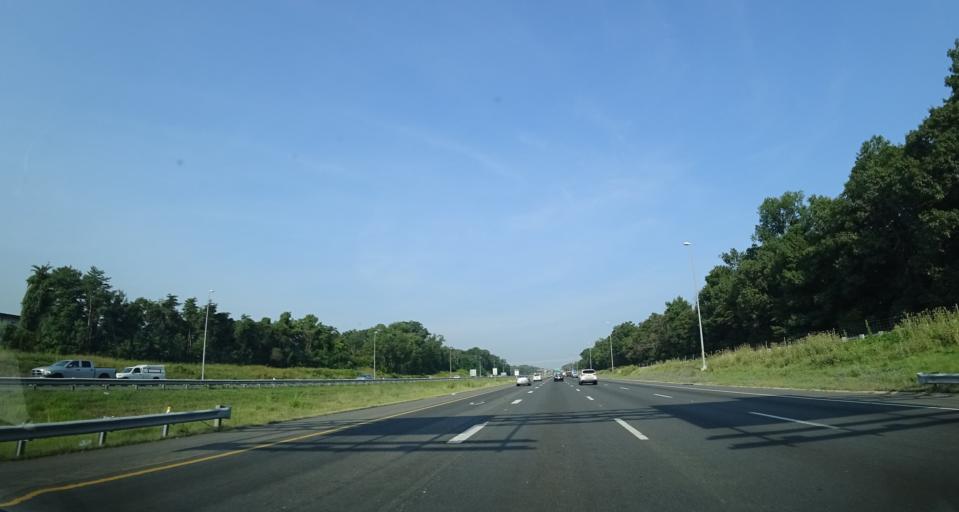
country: US
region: Virginia
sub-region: Prince William County
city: Bull Run
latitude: 38.7991
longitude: -77.5563
